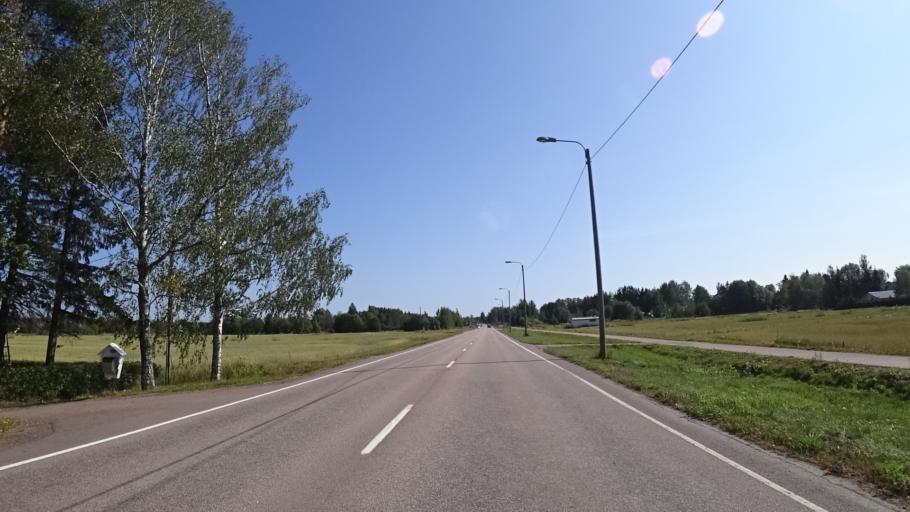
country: FI
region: Kymenlaakso
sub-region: Kotka-Hamina
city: Karhula
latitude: 60.5298
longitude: 26.9397
